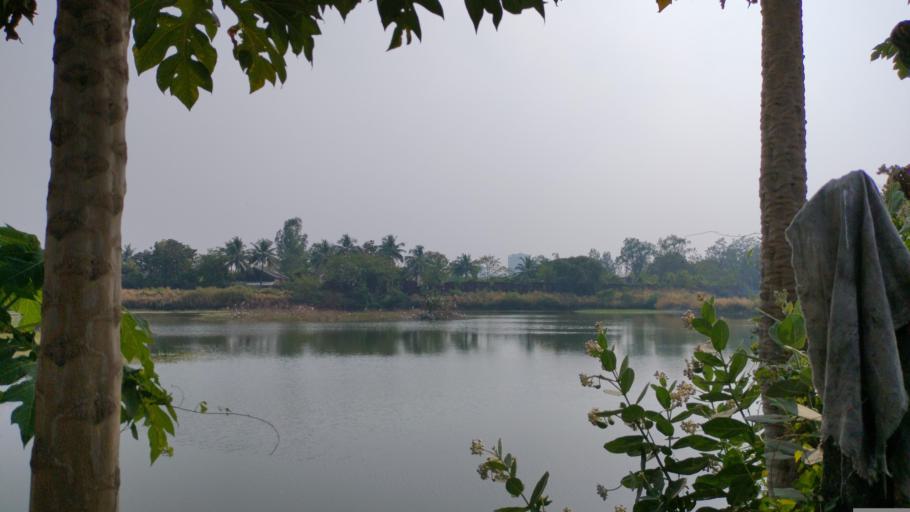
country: IN
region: Maharashtra
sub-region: Thane
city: Navi Mumbai
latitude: 19.0700
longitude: 73.0173
